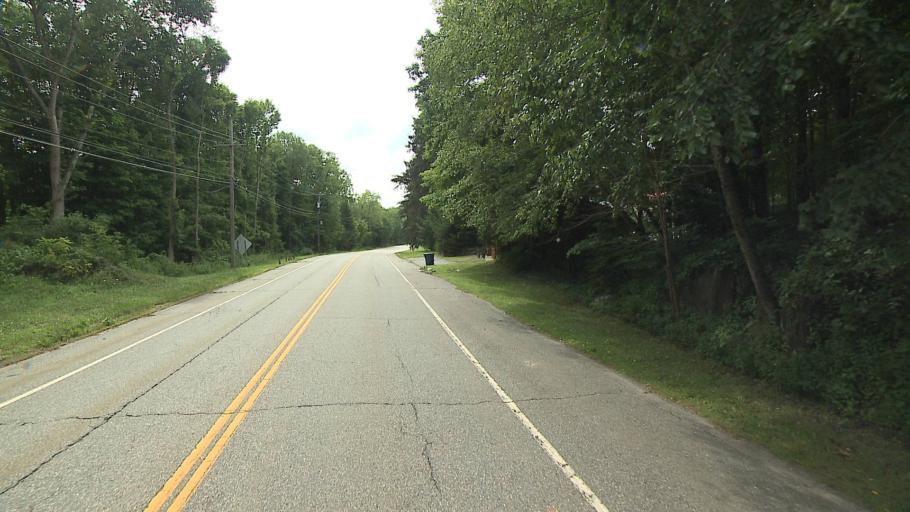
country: US
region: Connecticut
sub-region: Litchfield County
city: New Preston
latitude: 41.6802
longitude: -73.3309
